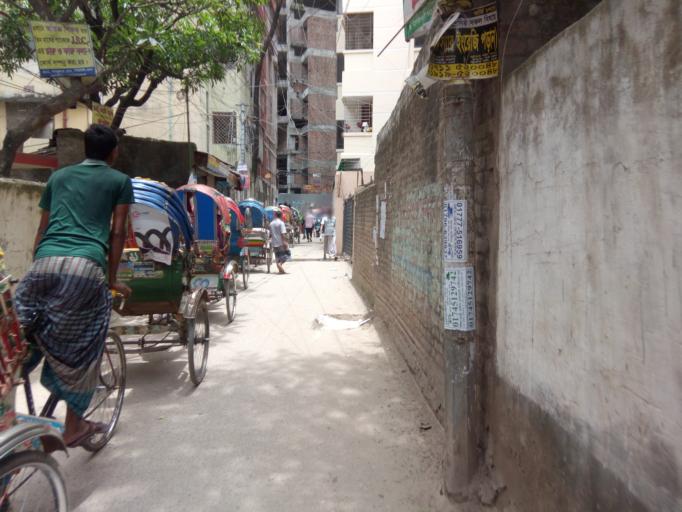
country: BD
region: Dhaka
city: Azimpur
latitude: 23.7421
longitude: 90.3907
